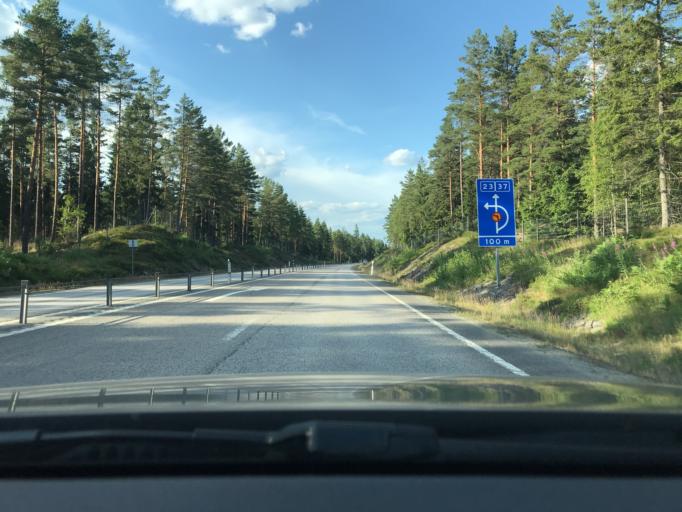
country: SE
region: Kronoberg
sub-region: Vaxjo Kommun
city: Braas
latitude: 57.0252
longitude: 15.0598
